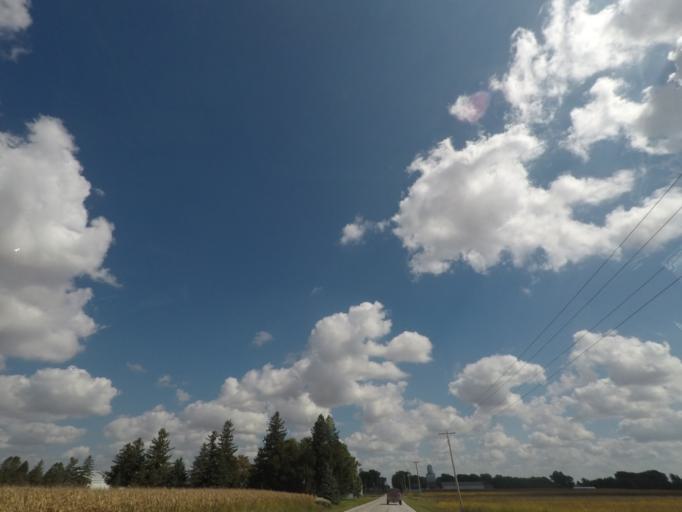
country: US
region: Iowa
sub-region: Story County
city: Nevada
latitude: 42.0706
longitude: -93.4022
